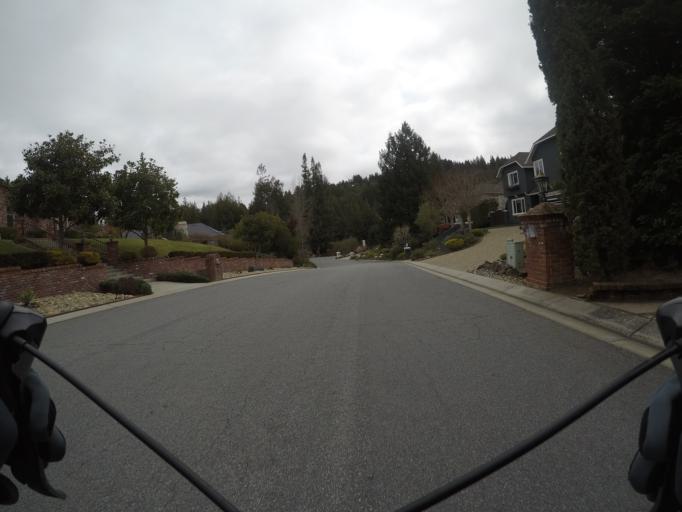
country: US
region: California
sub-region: Santa Cruz County
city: Scotts Valley
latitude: 37.0545
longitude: -121.9961
